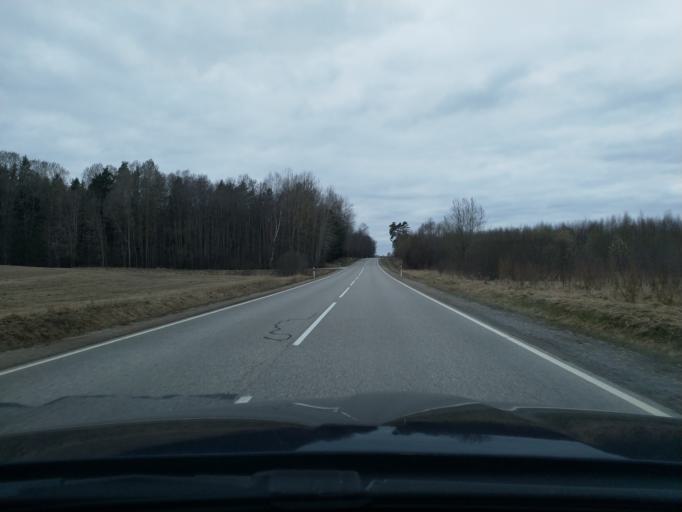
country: LV
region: Kuldigas Rajons
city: Kuldiga
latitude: 56.9679
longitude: 22.0530
